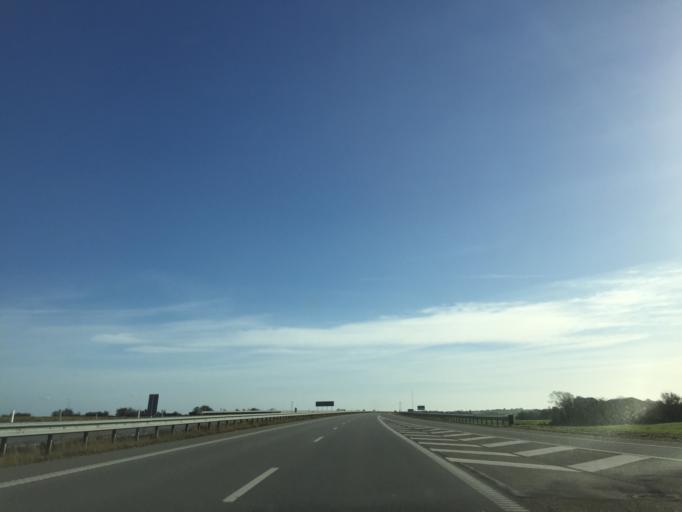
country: DK
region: South Denmark
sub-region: Sonderborg Kommune
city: Dybbol
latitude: 54.9337
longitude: 9.6981
